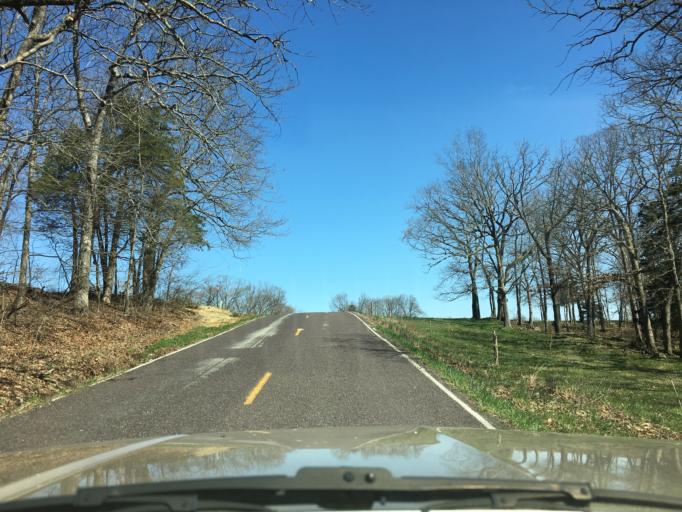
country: US
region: Missouri
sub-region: Franklin County
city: New Haven
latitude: 38.5438
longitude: -91.3303
